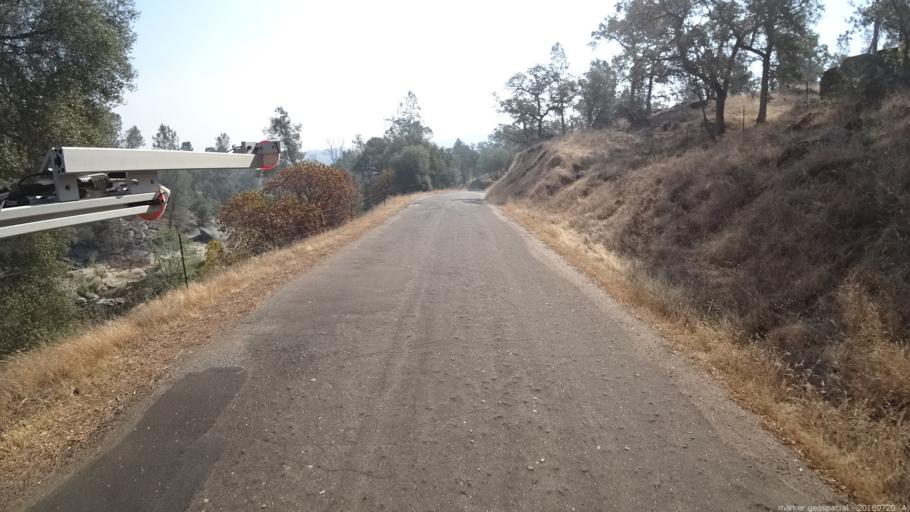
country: US
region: California
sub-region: Madera County
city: Yosemite Lakes
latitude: 37.2727
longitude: -119.8791
